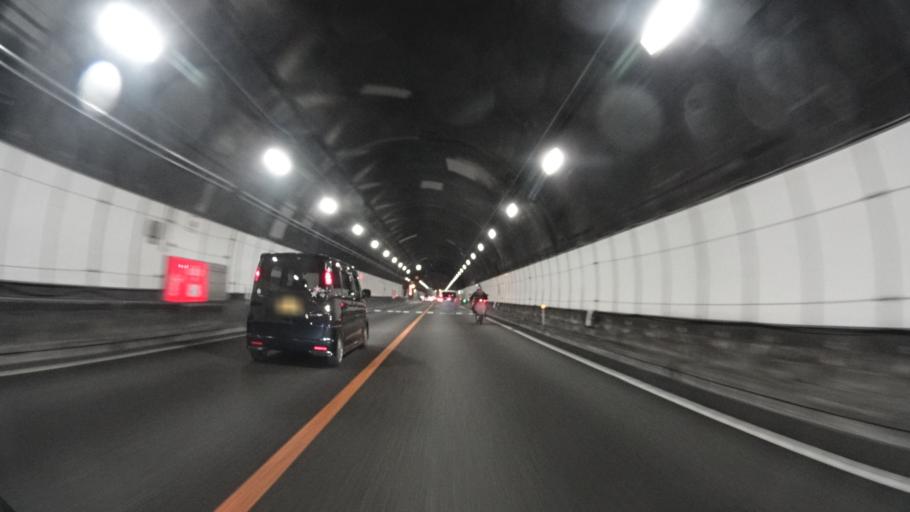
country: JP
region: Shizuoka
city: Gotemba
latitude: 35.3694
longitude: 139.0512
